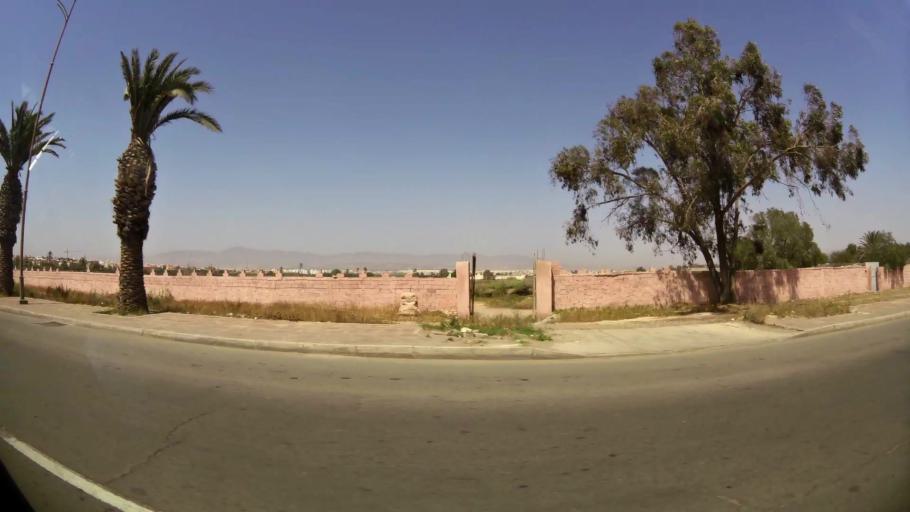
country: MA
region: Souss-Massa-Draa
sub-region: Inezgane-Ait Mellou
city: Inezgane
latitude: 30.3583
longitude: -9.5209
